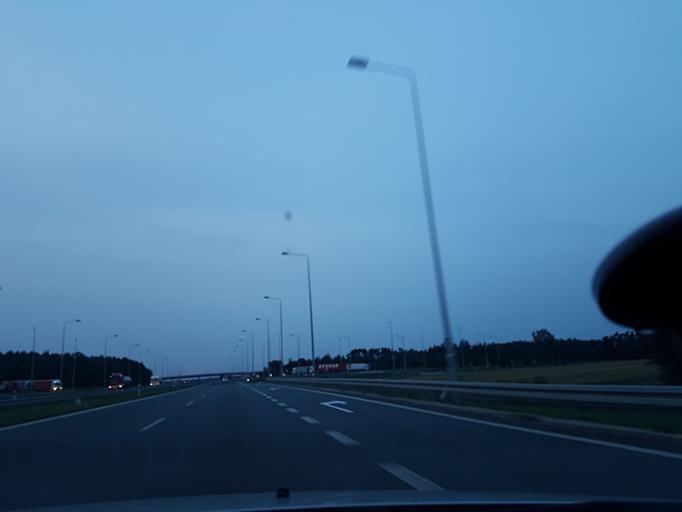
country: PL
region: Lodz Voivodeship
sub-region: Powiat leczycki
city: Piatek
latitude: 52.0085
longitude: 19.5429
